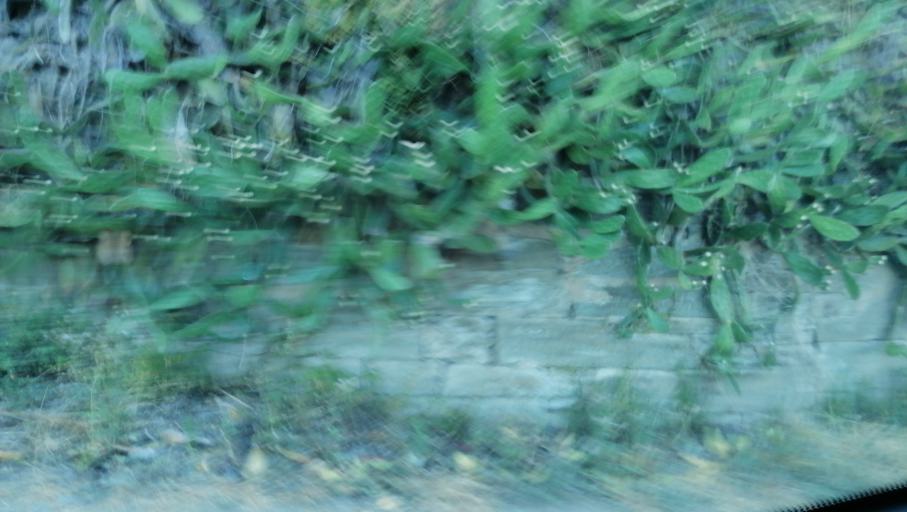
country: PT
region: Vila Real
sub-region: Sabrosa
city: Vilela
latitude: 41.1903
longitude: -7.5493
